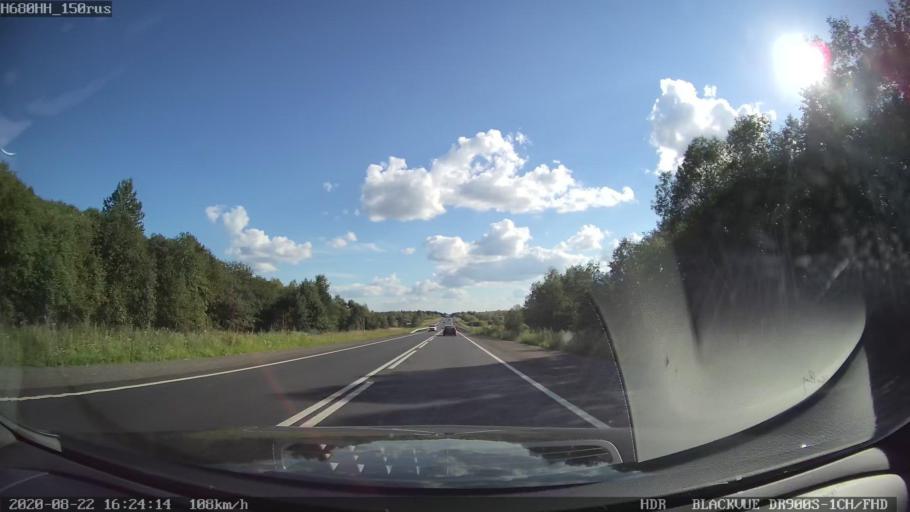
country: RU
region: Tverskaya
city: Rameshki
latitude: 57.3408
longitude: 36.0963
